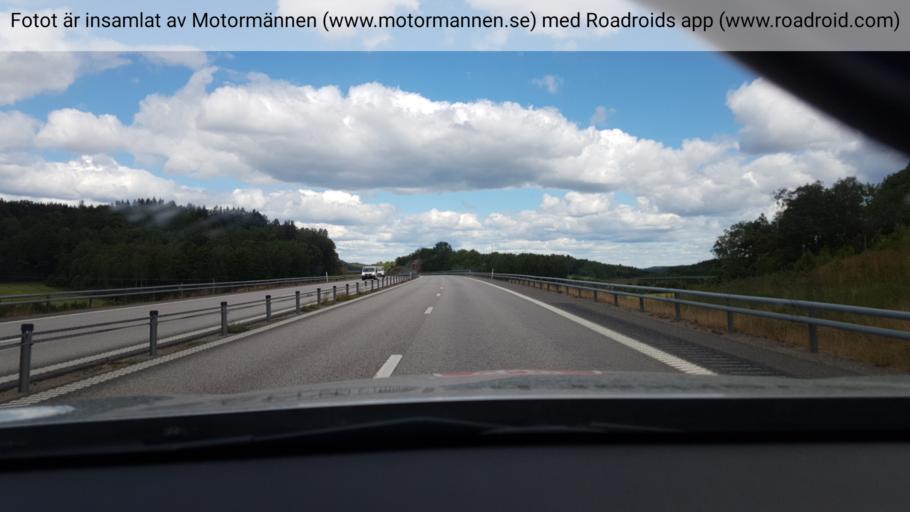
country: SE
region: Vaestra Goetaland
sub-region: Ale Kommun
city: Skepplanda
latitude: 58.0211
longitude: 12.1767
